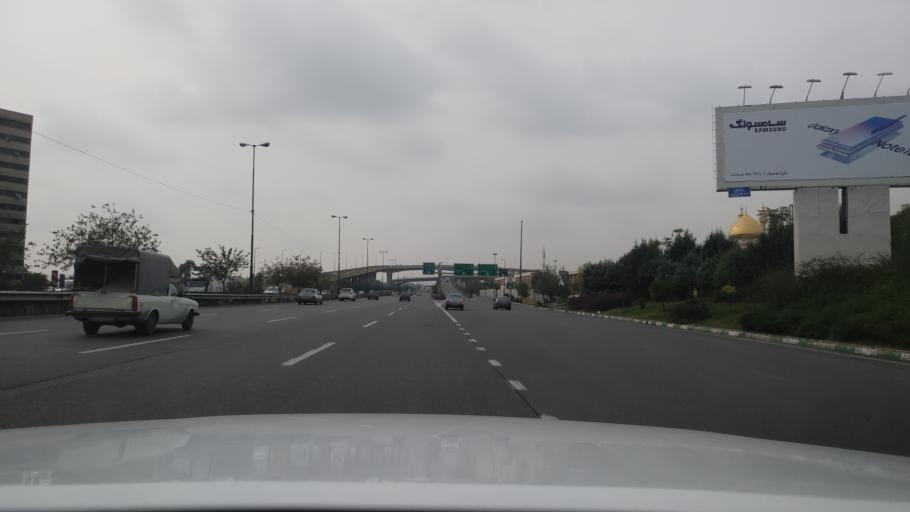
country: IR
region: Tehran
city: Tehran
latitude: 35.7172
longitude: 51.3054
